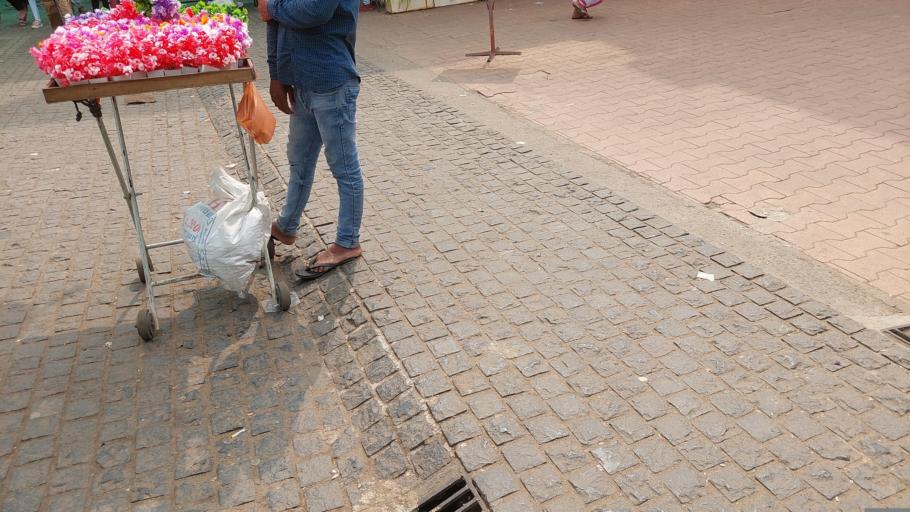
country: IN
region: Kerala
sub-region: Kozhikode
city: Kozhikode
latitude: 11.2497
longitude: 75.7817
